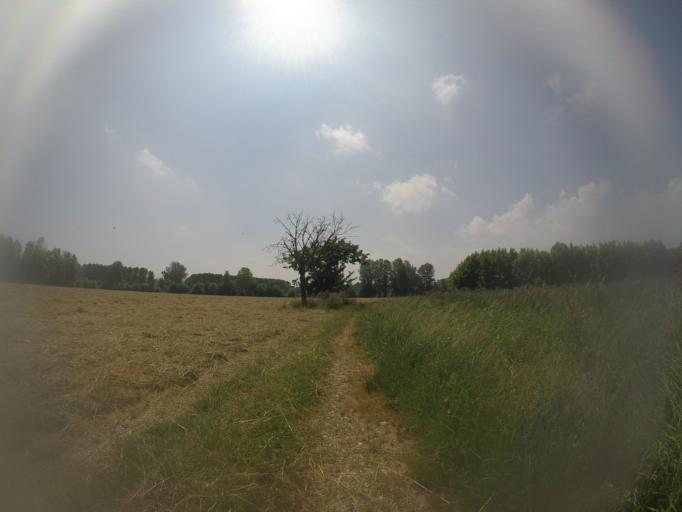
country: IT
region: Friuli Venezia Giulia
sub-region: Provincia di Udine
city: Bertiolo
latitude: 45.9322
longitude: 13.0364
